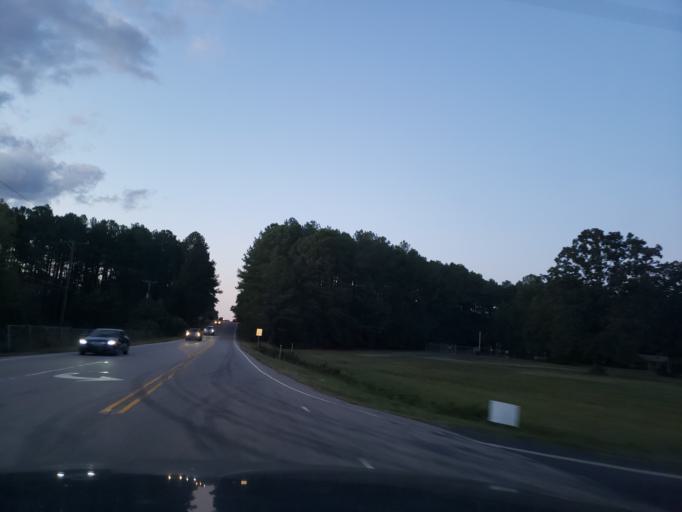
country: US
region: North Carolina
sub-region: Orange County
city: Chapel Hill
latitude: 35.8935
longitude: -78.9582
